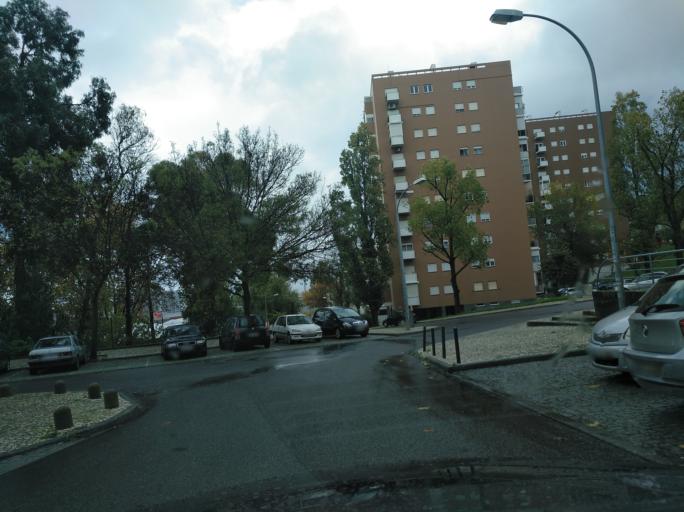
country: PT
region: Lisbon
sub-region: Loures
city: Moscavide
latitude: 38.7614
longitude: -9.1094
